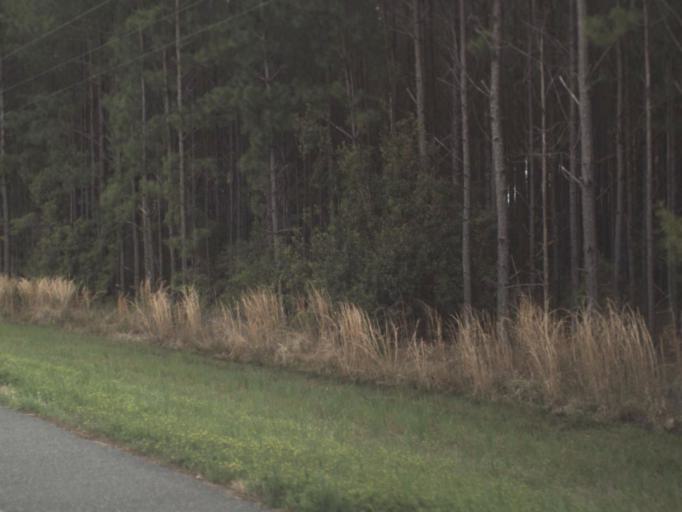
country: US
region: Florida
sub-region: Calhoun County
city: Blountstown
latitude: 30.3491
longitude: -85.2140
